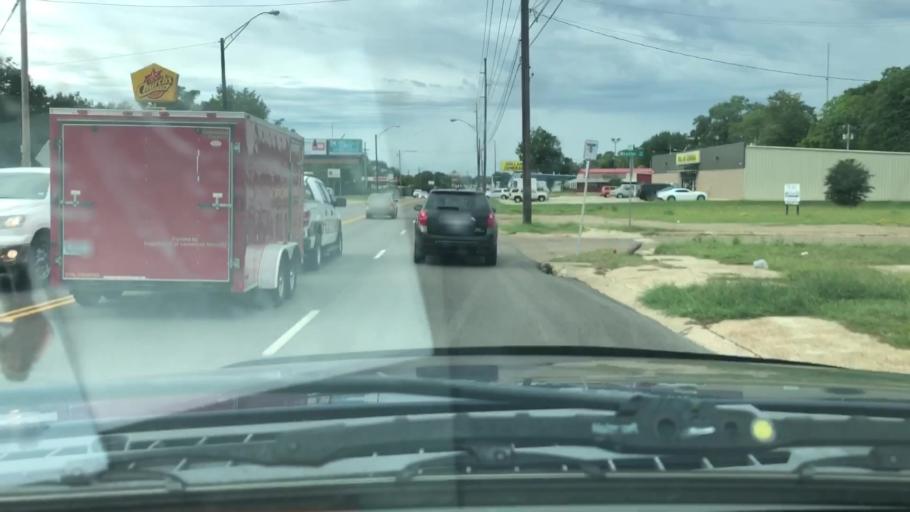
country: US
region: Texas
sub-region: Bowie County
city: Texarkana
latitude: 33.4350
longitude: -94.0687
